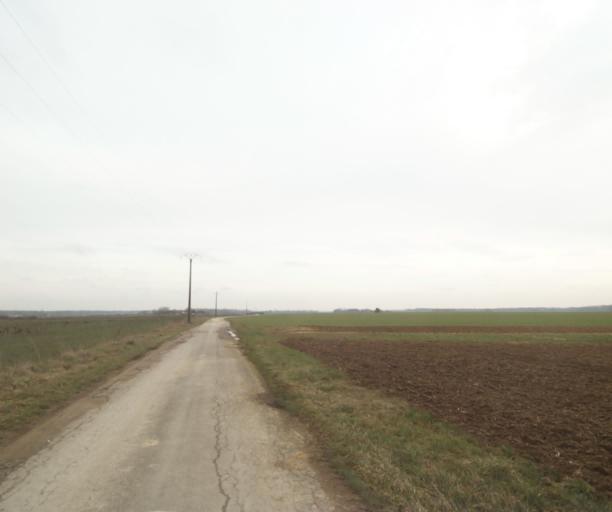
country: FR
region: Champagne-Ardenne
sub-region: Departement de la Haute-Marne
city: Villiers-en-Lieu
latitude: 48.6765
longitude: 4.8639
